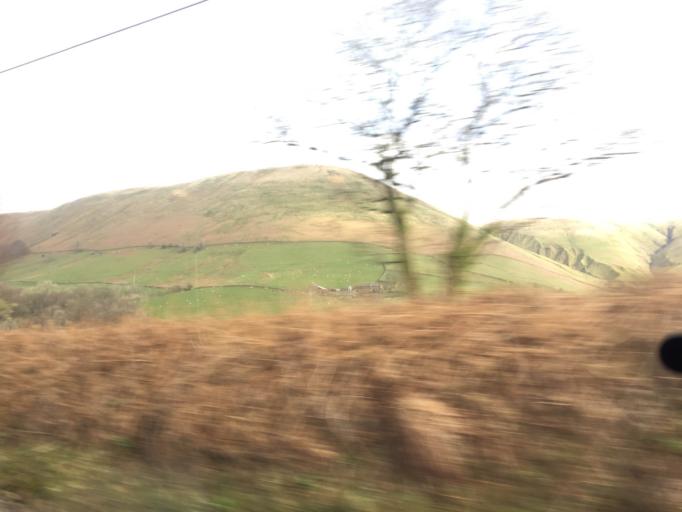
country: GB
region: England
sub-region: Cumbria
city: Sedbergh
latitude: 54.3870
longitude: -2.5855
